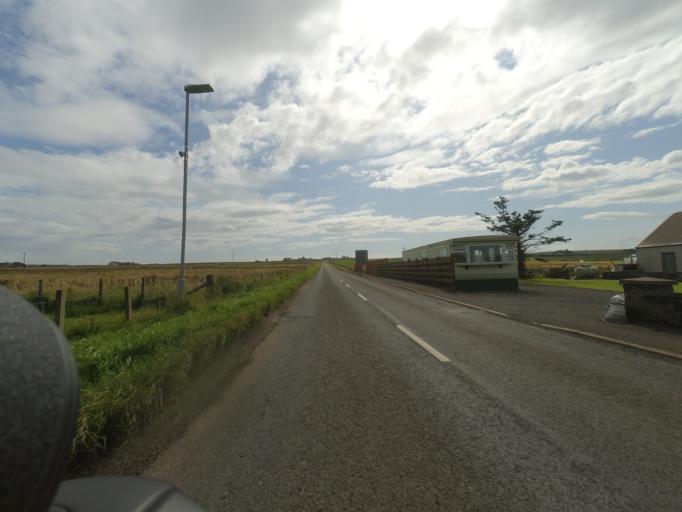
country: GB
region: Scotland
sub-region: Highland
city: Wick
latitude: 58.6362
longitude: -3.0690
